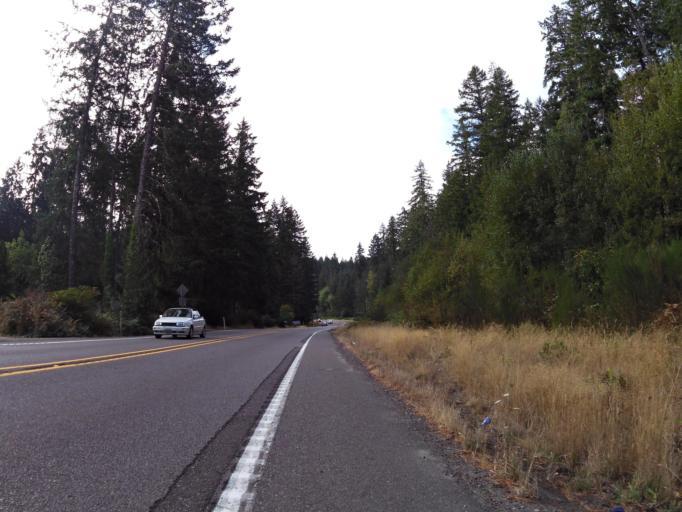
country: US
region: Washington
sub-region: Mason County
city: Allyn
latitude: 47.4085
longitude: -122.8395
